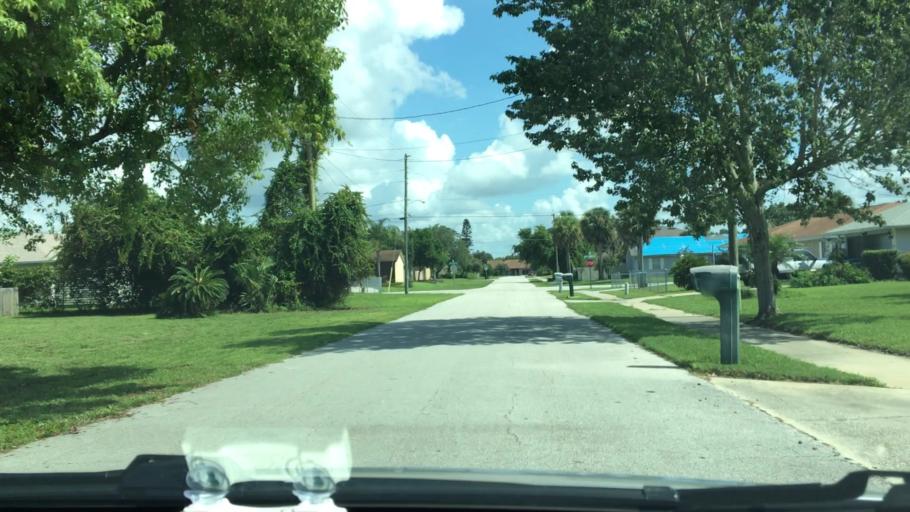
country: US
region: Florida
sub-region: Volusia County
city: Deltona
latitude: 28.8794
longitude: -81.2325
